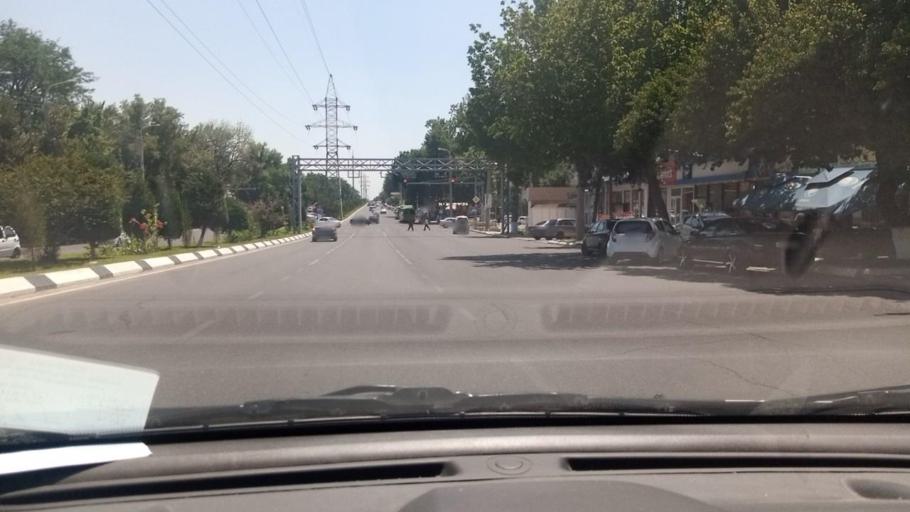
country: UZ
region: Toshkent Shahri
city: Tashkent
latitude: 41.2987
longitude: 69.1939
